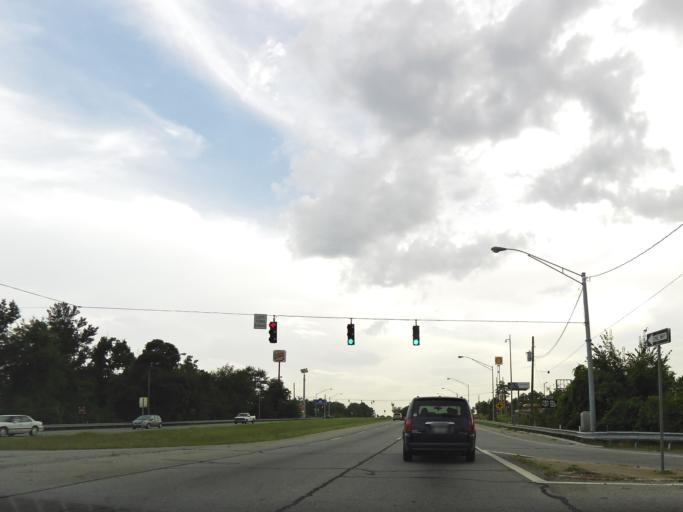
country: US
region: Georgia
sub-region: Bibb County
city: West Point
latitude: 32.8094
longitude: -83.7266
